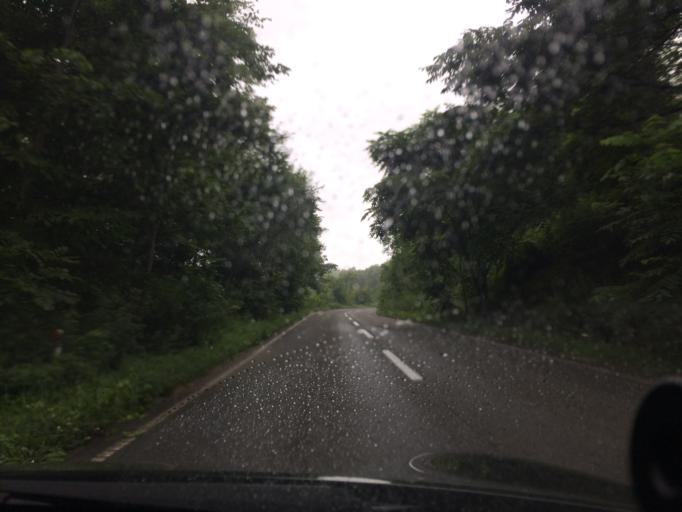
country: JP
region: Hokkaido
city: Otofuke
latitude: 43.0107
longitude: 143.0767
